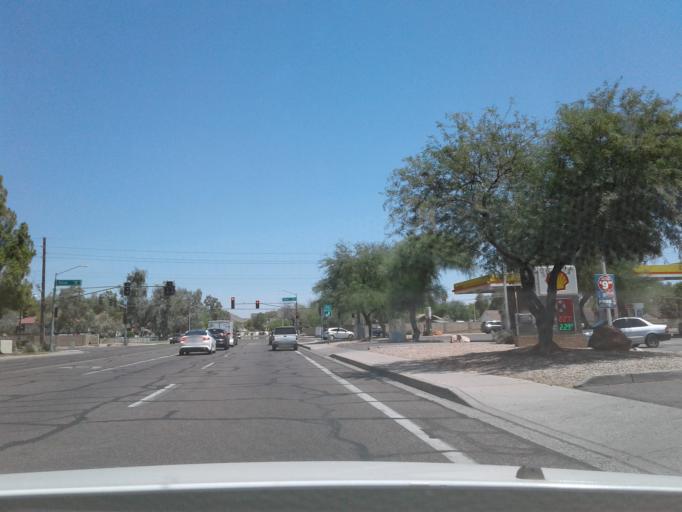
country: US
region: Arizona
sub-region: Maricopa County
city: Guadalupe
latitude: 33.3479
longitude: -111.9804
